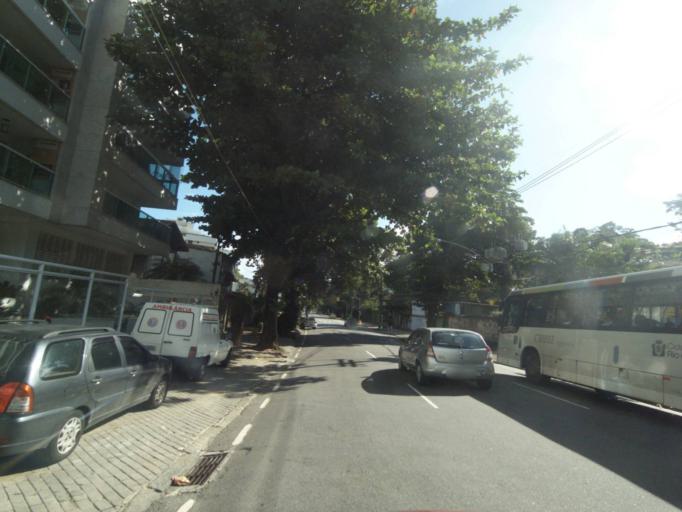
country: BR
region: Rio de Janeiro
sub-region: Rio De Janeiro
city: Rio de Janeiro
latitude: -22.9309
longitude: -43.3257
